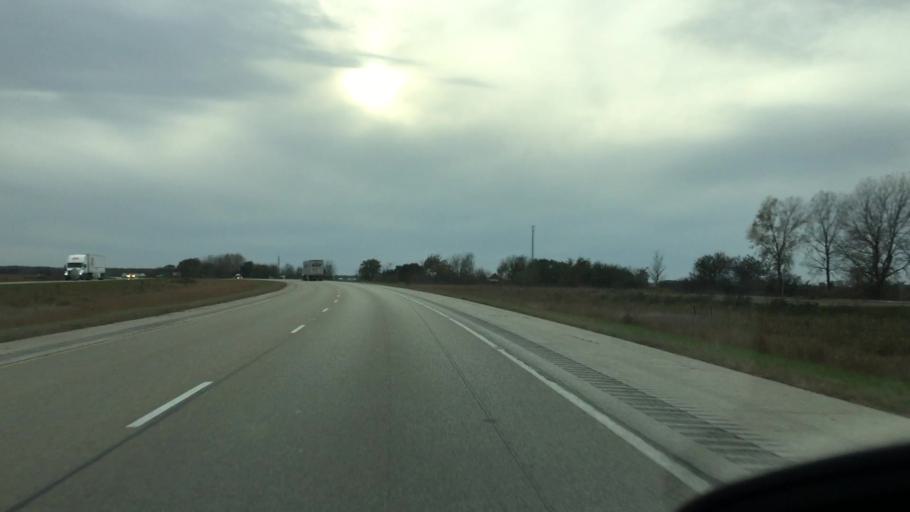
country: US
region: Illinois
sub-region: McLean County
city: Twin Grove
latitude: 40.3948
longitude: -89.0745
